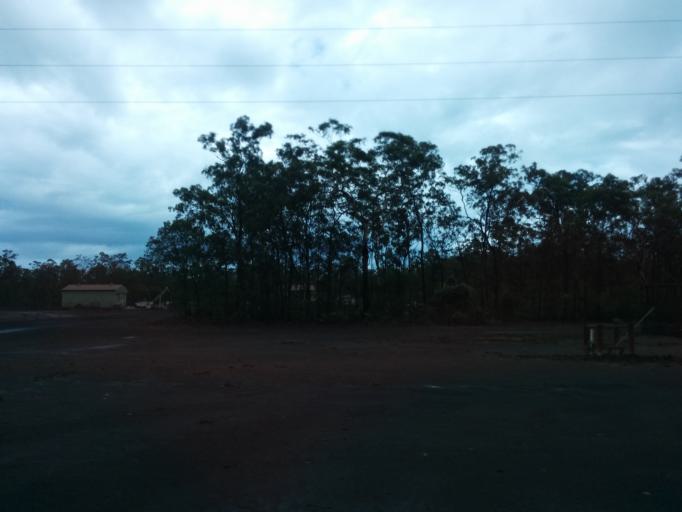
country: AU
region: Northern Territory
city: Alyangula
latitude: -13.9589
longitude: 136.4429
